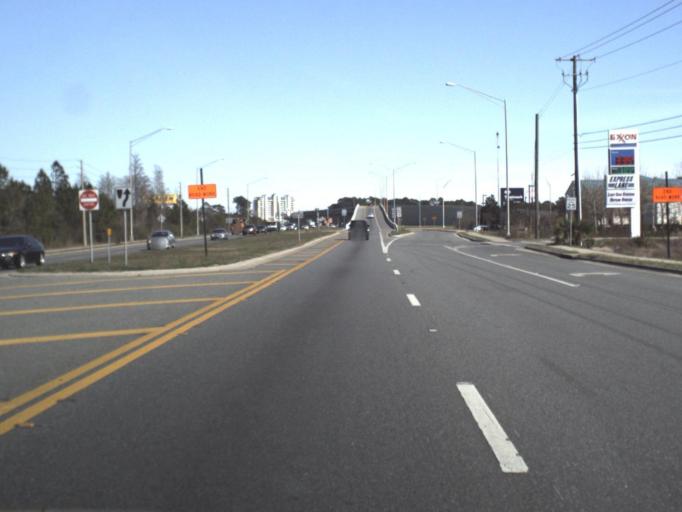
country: US
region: Florida
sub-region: Bay County
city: Upper Grand Lagoon
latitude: 30.1884
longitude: -85.7693
